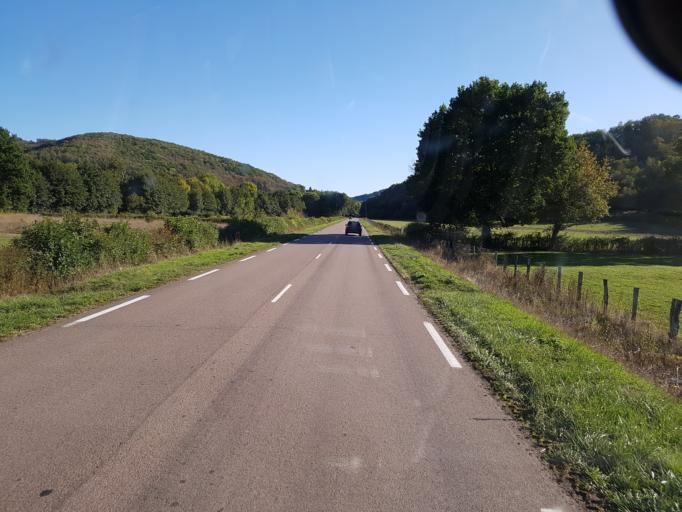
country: FR
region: Bourgogne
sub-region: Departement de la Cote-d'Or
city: Saulieu
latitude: 47.1095
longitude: 4.2285
